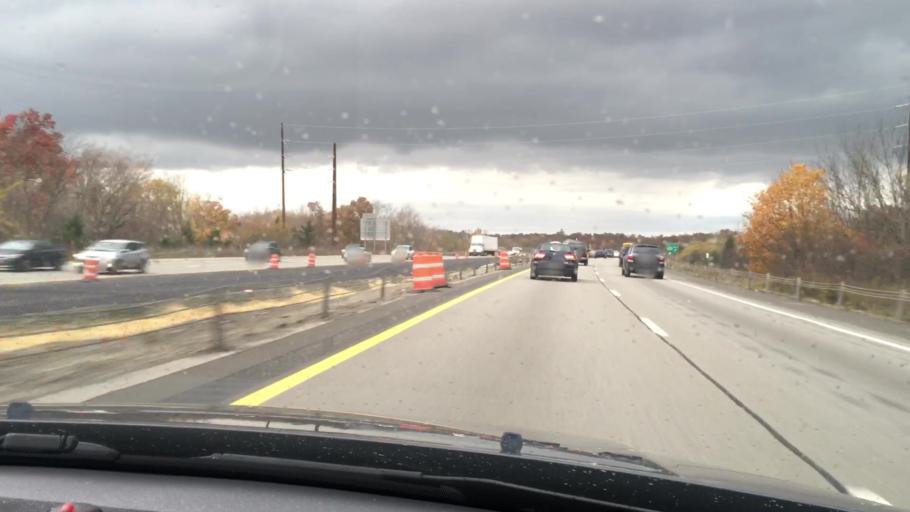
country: US
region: New York
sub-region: Dutchess County
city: Fishkill
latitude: 41.5243
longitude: -73.9105
